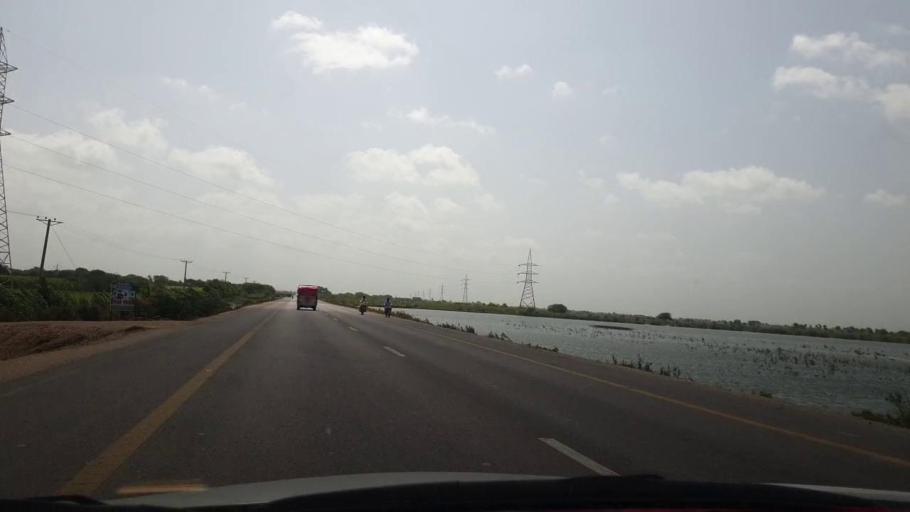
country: PK
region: Sindh
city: Talhar
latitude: 24.9251
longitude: 68.7189
